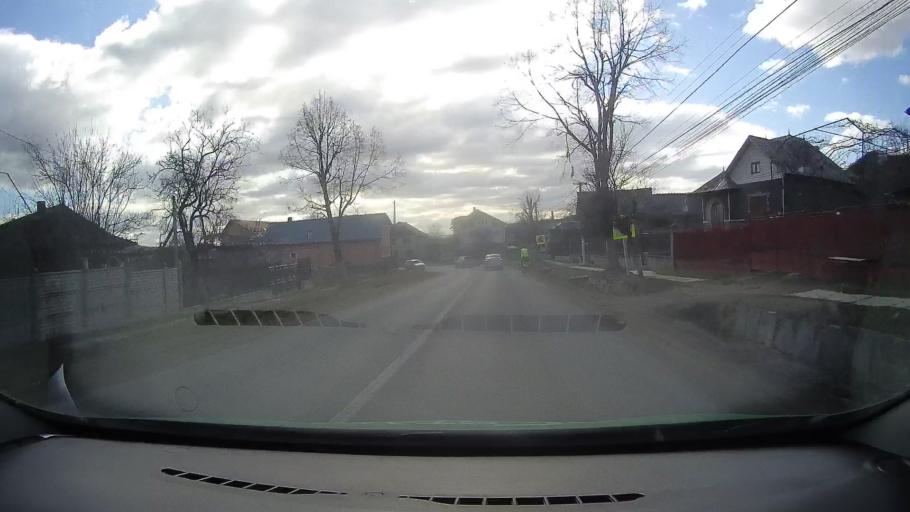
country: RO
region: Dambovita
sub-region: Comuna Motaeni
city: Motaeni
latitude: 45.0954
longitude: 25.4182
